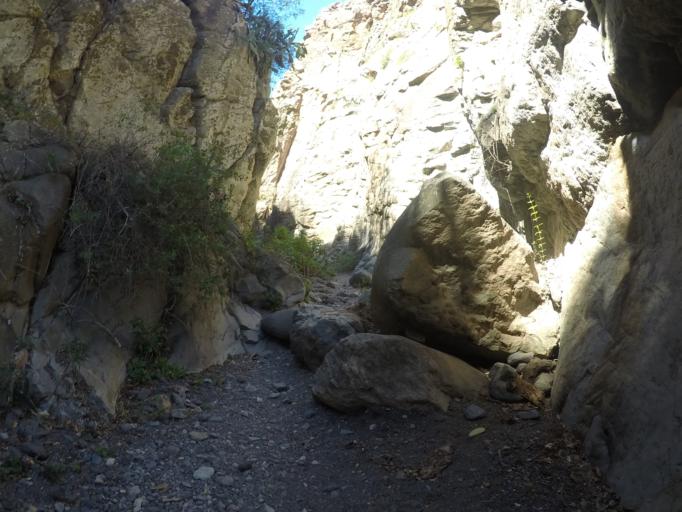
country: ES
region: Canary Islands
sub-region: Provincia de Santa Cruz de Tenerife
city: Lomo de Arico
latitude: 28.1848
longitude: -16.4919
